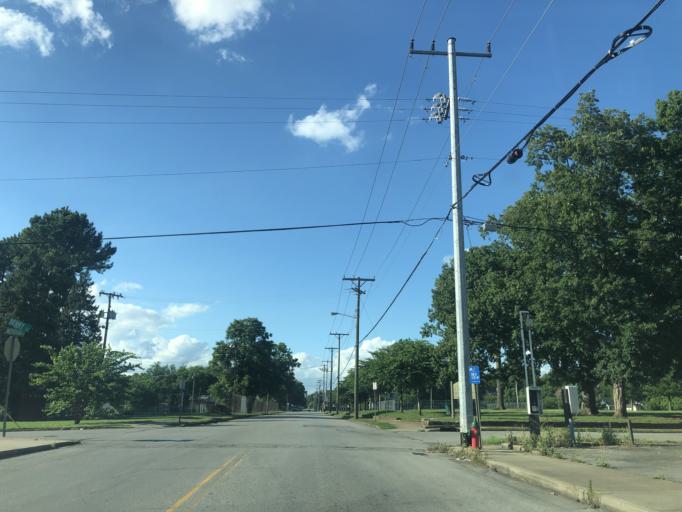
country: US
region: Tennessee
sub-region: Davidson County
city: Nashville
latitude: 36.1809
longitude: -86.7689
